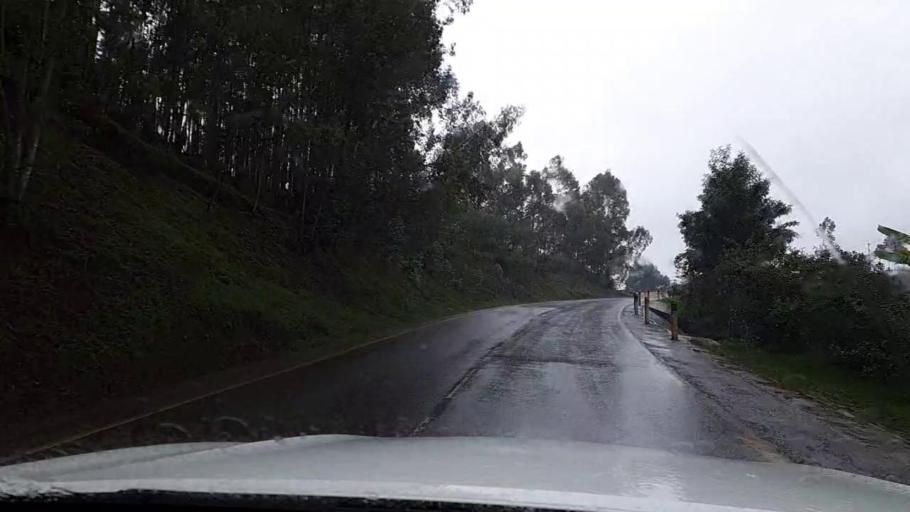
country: RW
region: Western Province
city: Cyangugu
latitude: -2.4623
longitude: 29.0009
